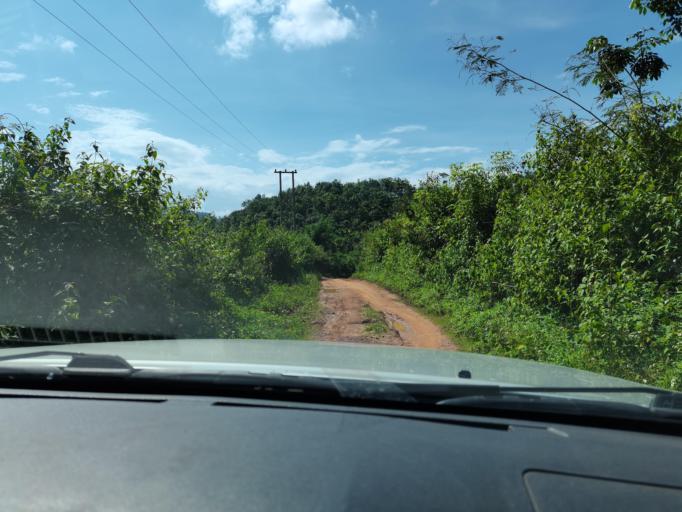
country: LA
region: Loungnamtha
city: Muang Nale
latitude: 20.5559
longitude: 101.0638
